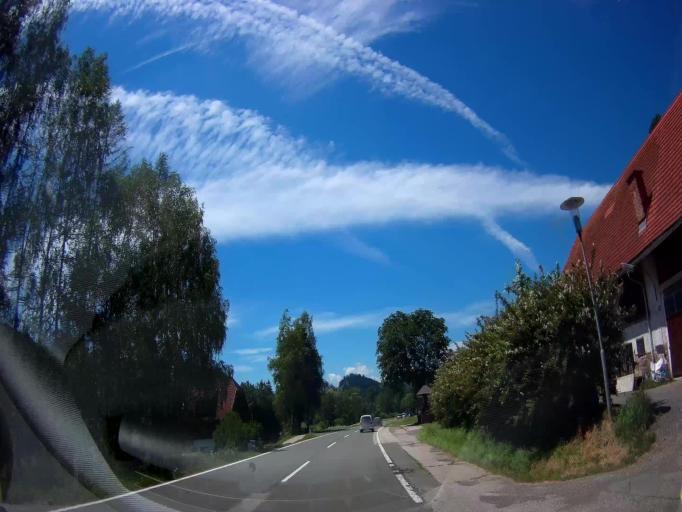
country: AT
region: Carinthia
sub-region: Politischer Bezirk Sankt Veit an der Glan
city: Micheldorf
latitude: 46.9012
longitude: 14.3782
